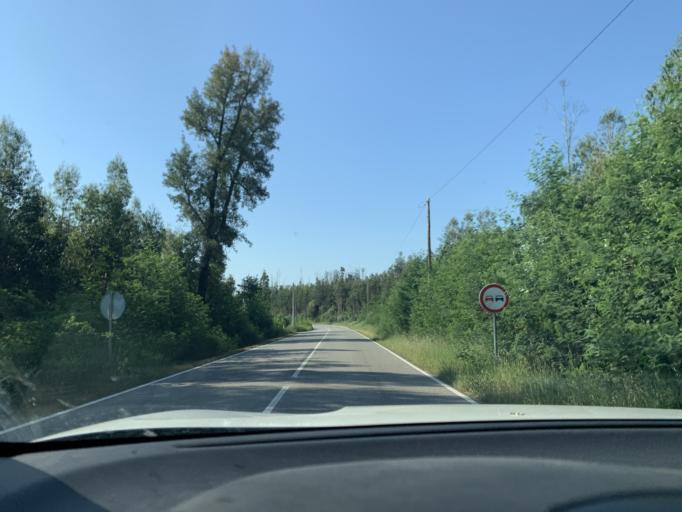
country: PT
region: Viseu
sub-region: Santa Comba Dao
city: Santa Comba Dao
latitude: 40.4524
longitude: -8.1031
